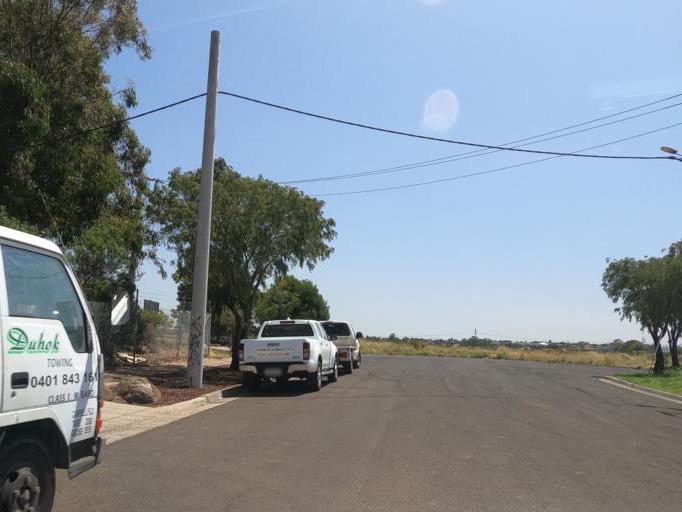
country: AU
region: Victoria
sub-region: Whittlesea
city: Epping
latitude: -37.6439
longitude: 145.0127
